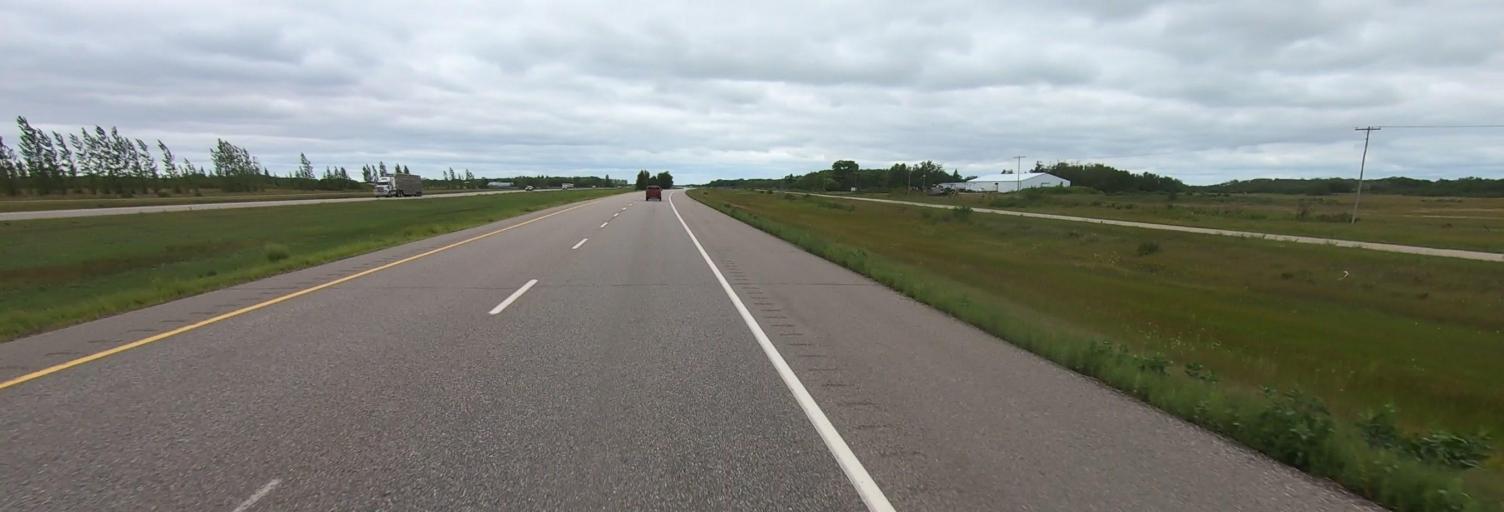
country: CA
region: Manitoba
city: Portage la Prairie
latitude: 49.9752
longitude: -98.6552
